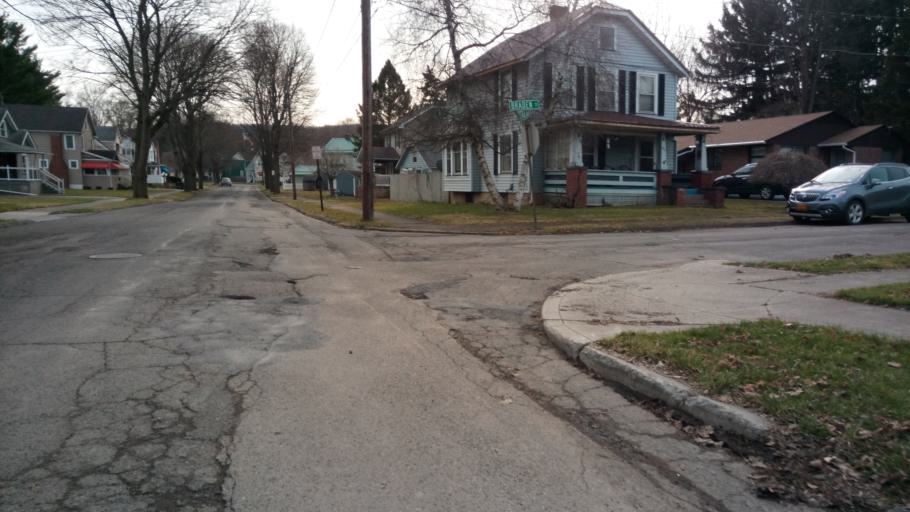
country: US
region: New York
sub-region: Chemung County
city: Elmira Heights
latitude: 42.1133
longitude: -76.8252
